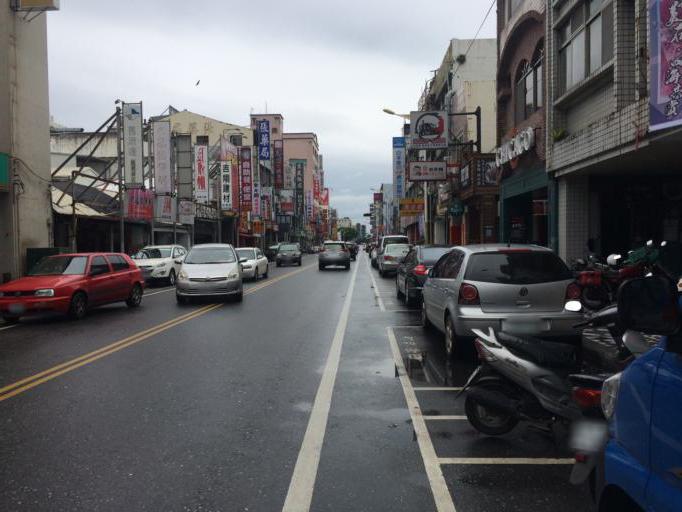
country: TW
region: Taiwan
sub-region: Hualien
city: Hualian
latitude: 23.9760
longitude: 121.6102
